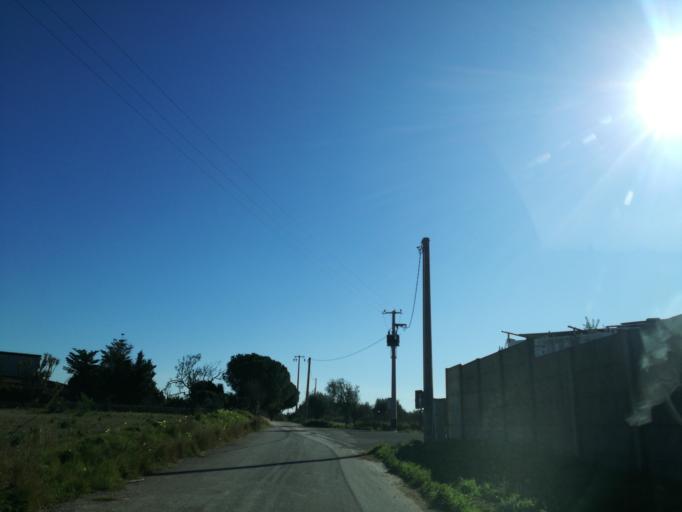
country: IT
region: Sicily
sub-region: Provincia di Caltanissetta
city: Niscemi
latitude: 37.0590
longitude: 14.3577
